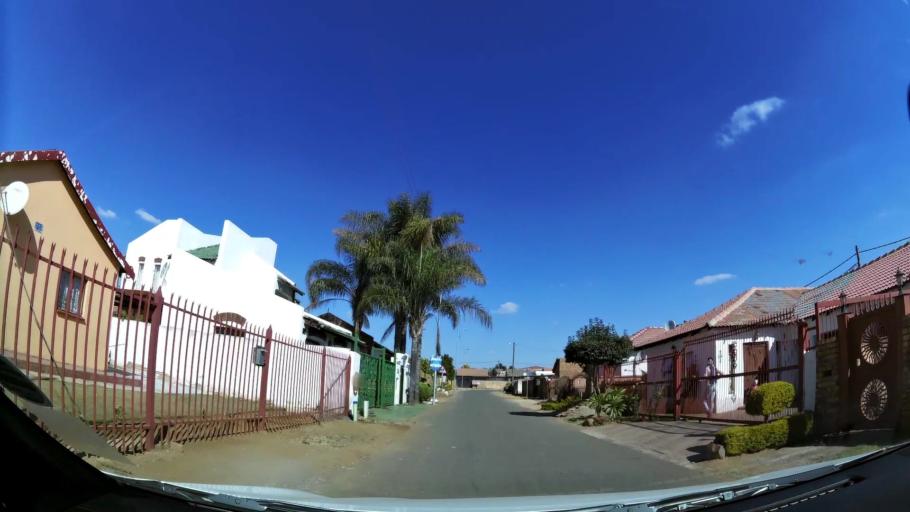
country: ZA
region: Gauteng
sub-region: City of Tshwane Metropolitan Municipality
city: Cullinan
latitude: -25.7162
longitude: 28.3994
